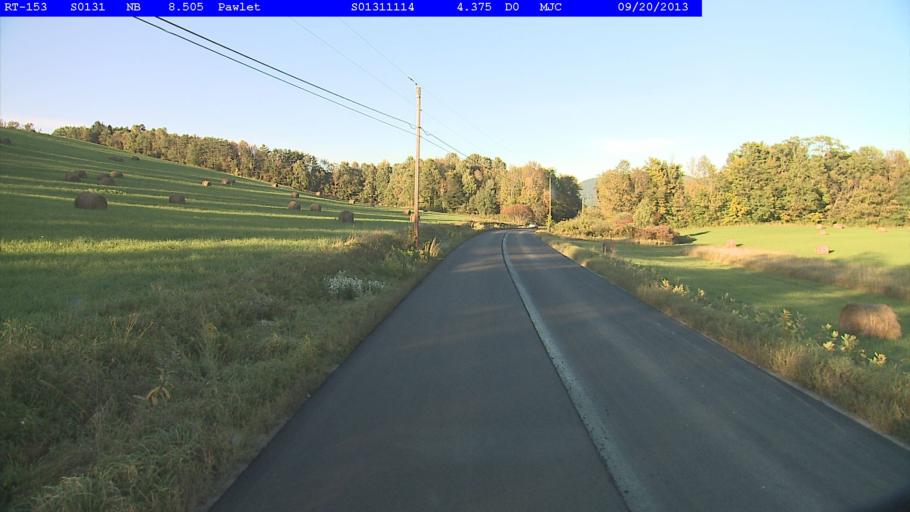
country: US
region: New York
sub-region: Washington County
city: Granville
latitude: 43.3694
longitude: -73.2345
